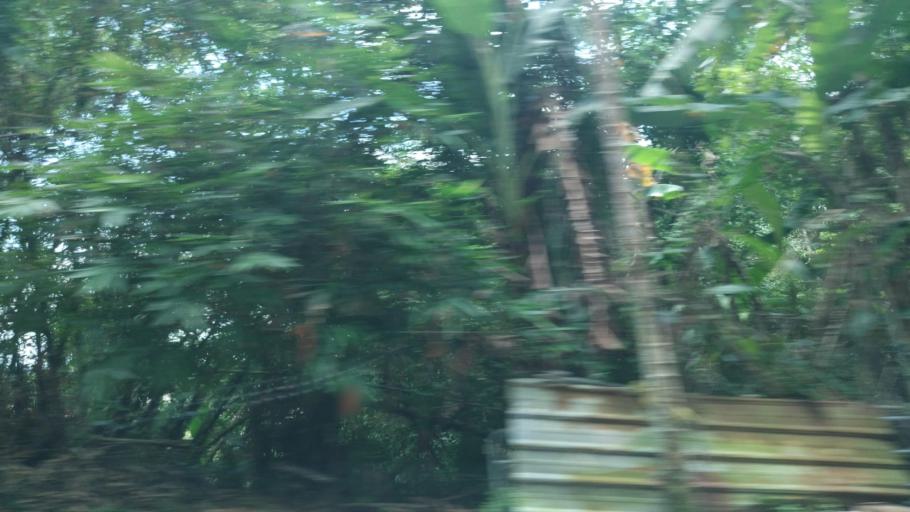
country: TW
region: Taiwan
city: Daxi
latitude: 24.9071
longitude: 121.4017
